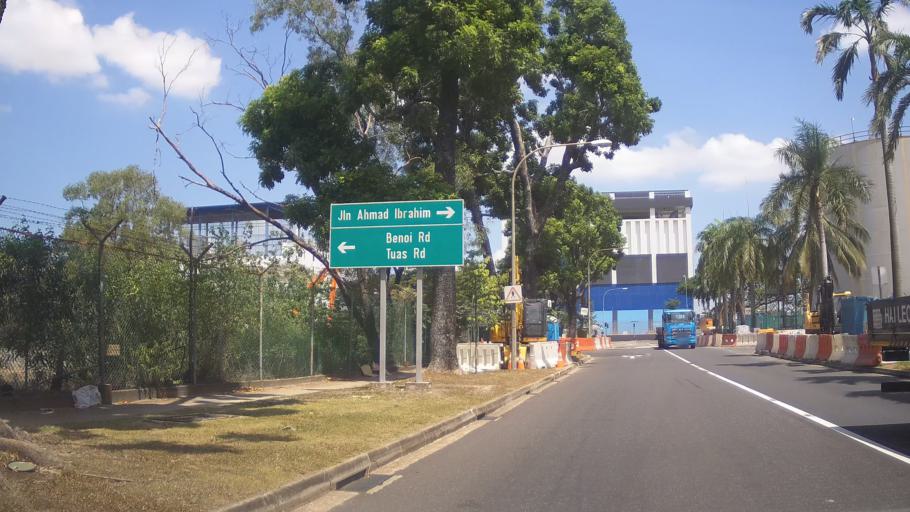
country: SG
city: Singapore
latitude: 1.3097
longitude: 103.6821
